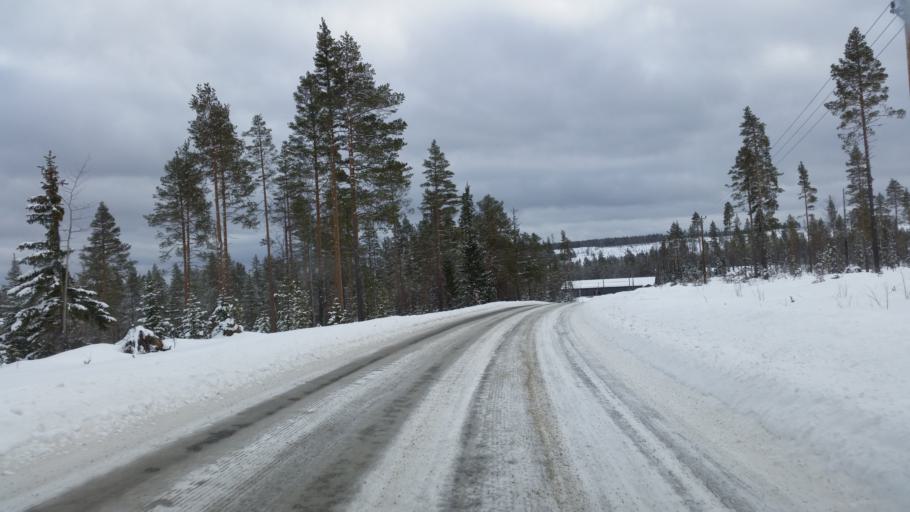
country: SE
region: Jaemtland
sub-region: Bergs Kommun
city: Hoverberg
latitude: 62.4750
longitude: 14.2587
